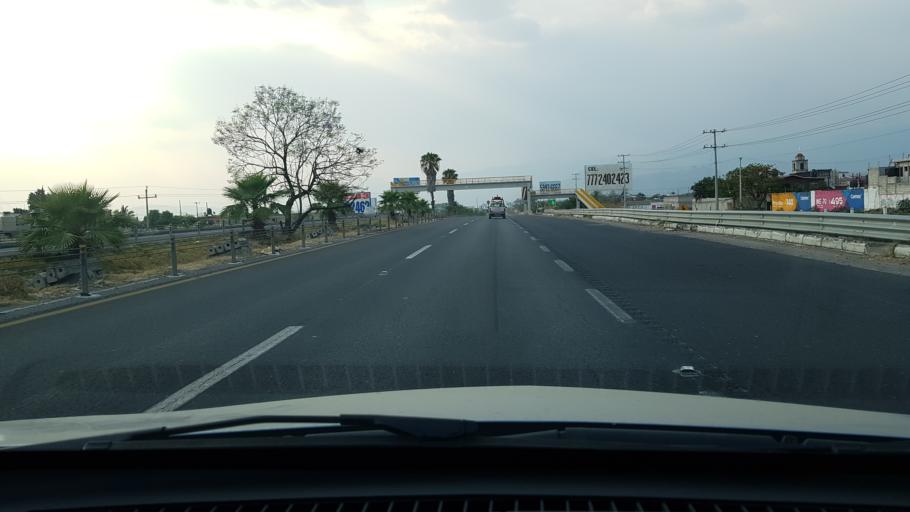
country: MX
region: Morelos
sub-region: Cuautla
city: Tierra Larga (Campo Nuevo)
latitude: 18.8554
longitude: -98.9408
